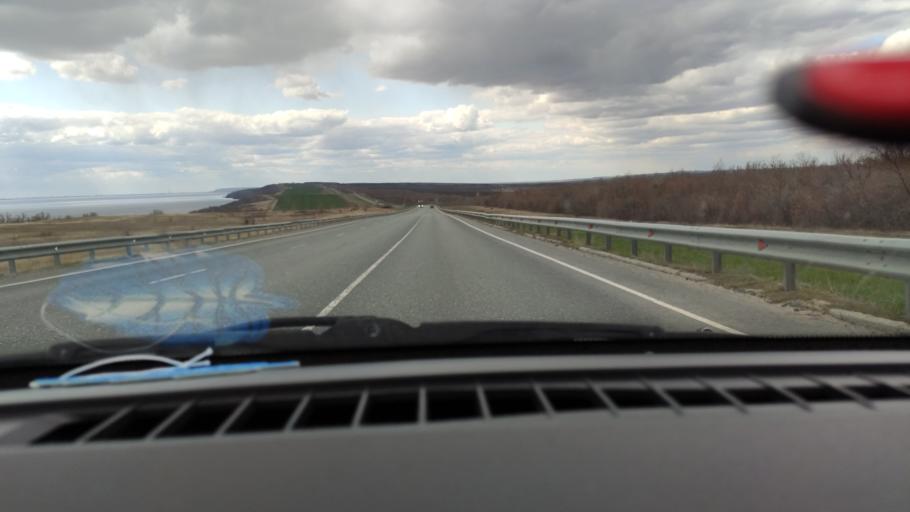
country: RU
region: Saratov
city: Balakovo
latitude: 52.2014
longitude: 47.8654
